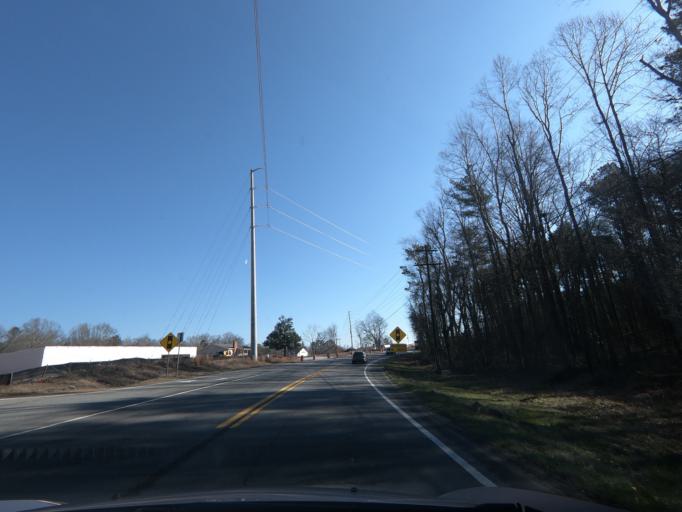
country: US
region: Georgia
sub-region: Forsyth County
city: Cumming
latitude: 34.2989
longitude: -84.1570
